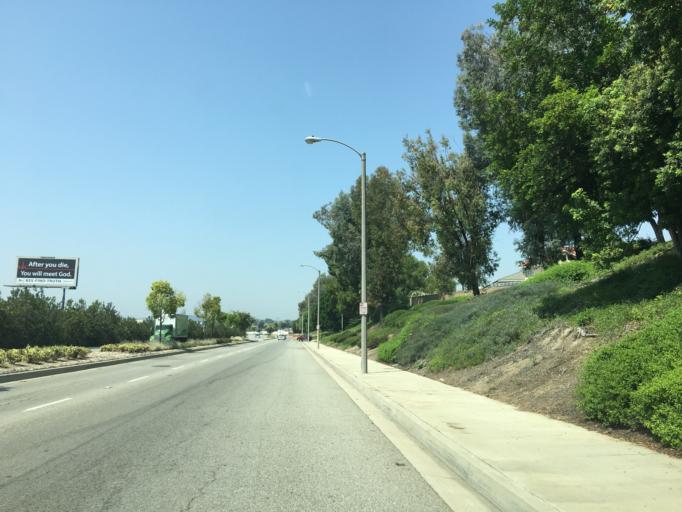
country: US
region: California
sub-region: Los Angeles County
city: Walnut
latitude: 34.0192
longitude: -117.8424
